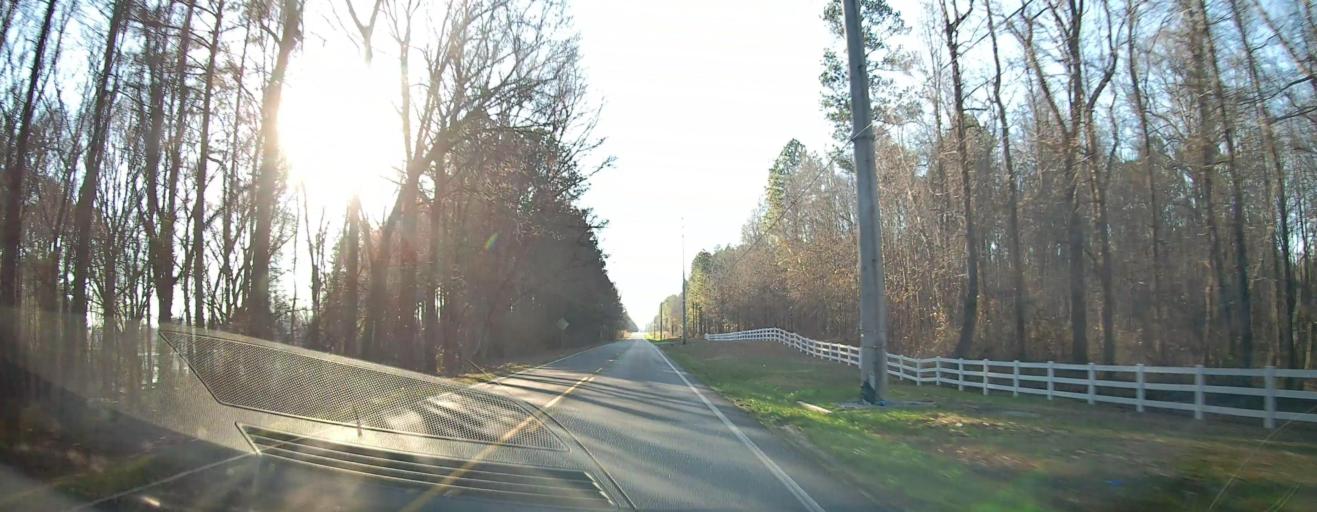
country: US
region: Georgia
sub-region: Harris County
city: Pine Mountain
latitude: 32.9162
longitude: -84.7810
